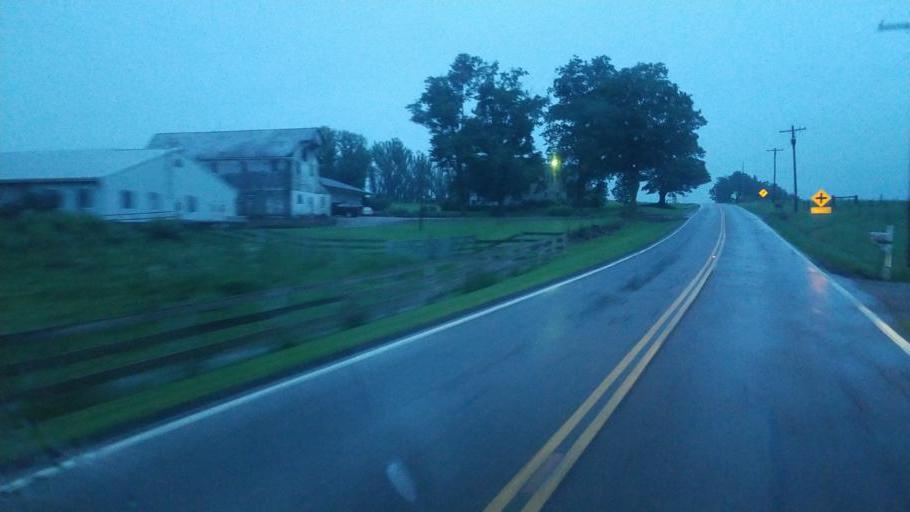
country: US
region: Ohio
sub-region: Knox County
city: Oak Hill
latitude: 40.3362
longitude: -82.1933
